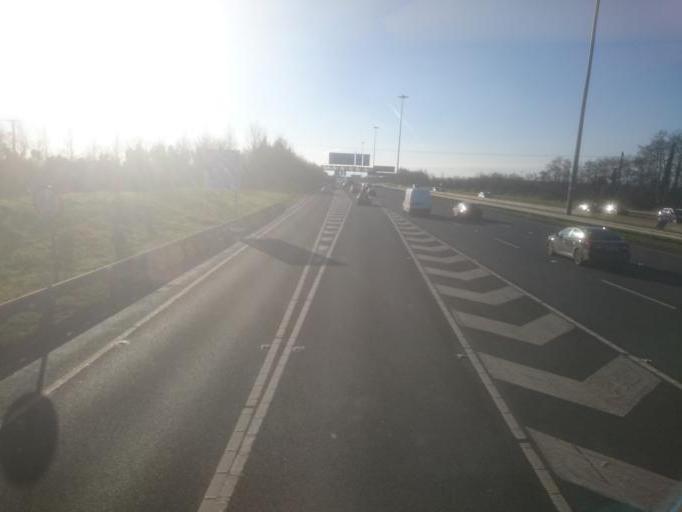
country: IE
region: Leinster
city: Kinsealy-Drinan
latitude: 53.4240
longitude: -6.2189
